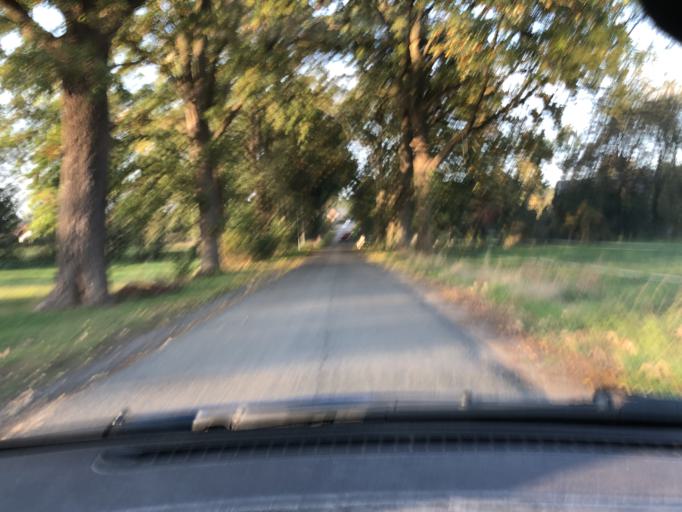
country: DE
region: Lower Saxony
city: Hitzacker
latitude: 53.1488
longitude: 11.0041
